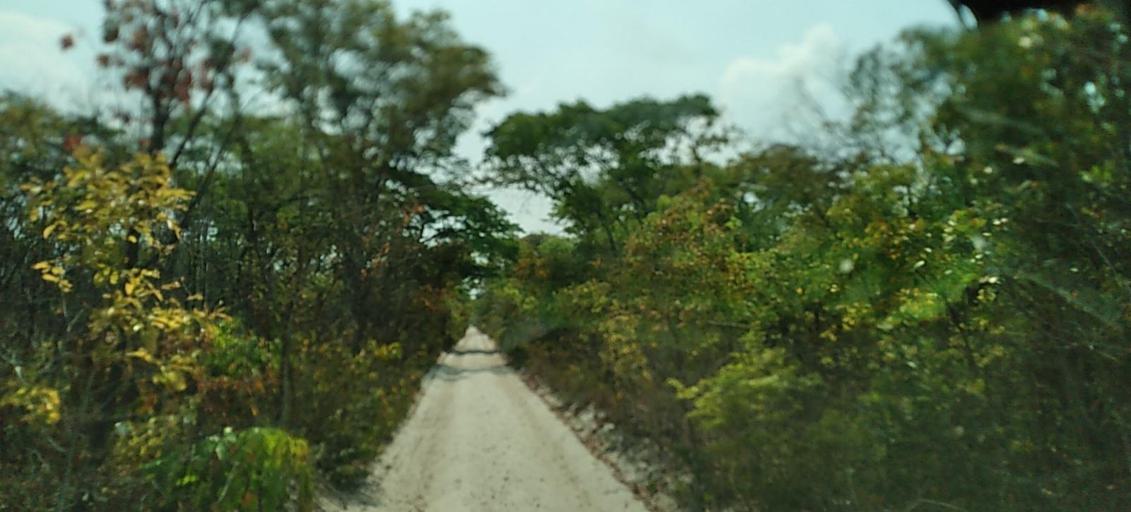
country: ZM
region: North-Western
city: Kabompo
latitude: -13.3893
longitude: 23.7794
